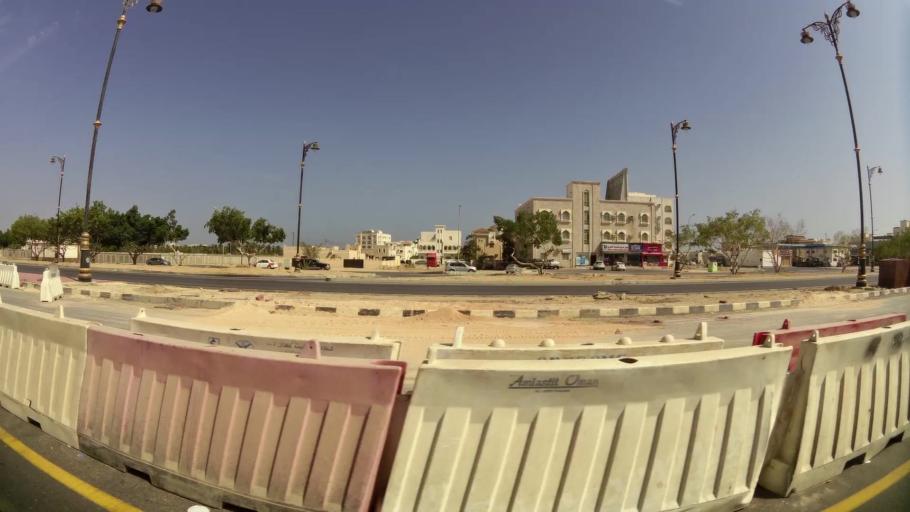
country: OM
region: Zufar
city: Salalah
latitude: 17.0226
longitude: 54.0691
